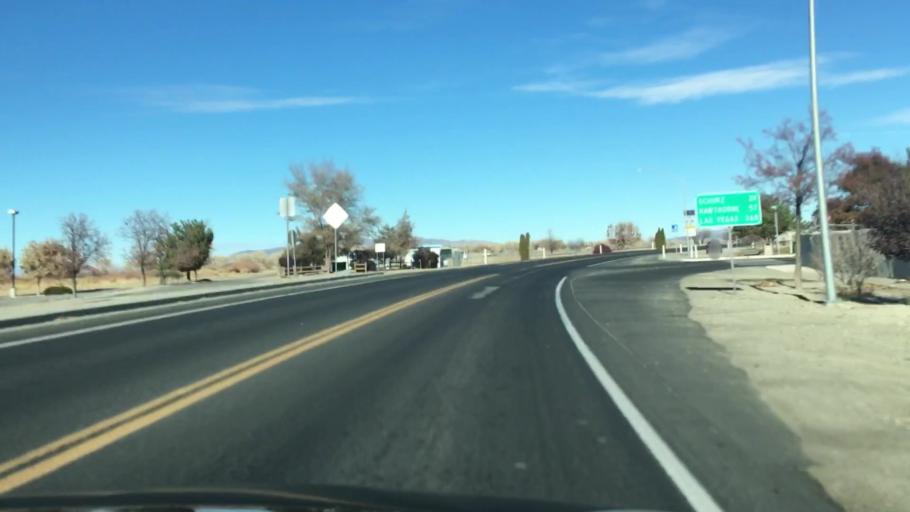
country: US
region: Nevada
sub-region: Lyon County
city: Yerington
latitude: 38.9947
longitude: -119.1630
